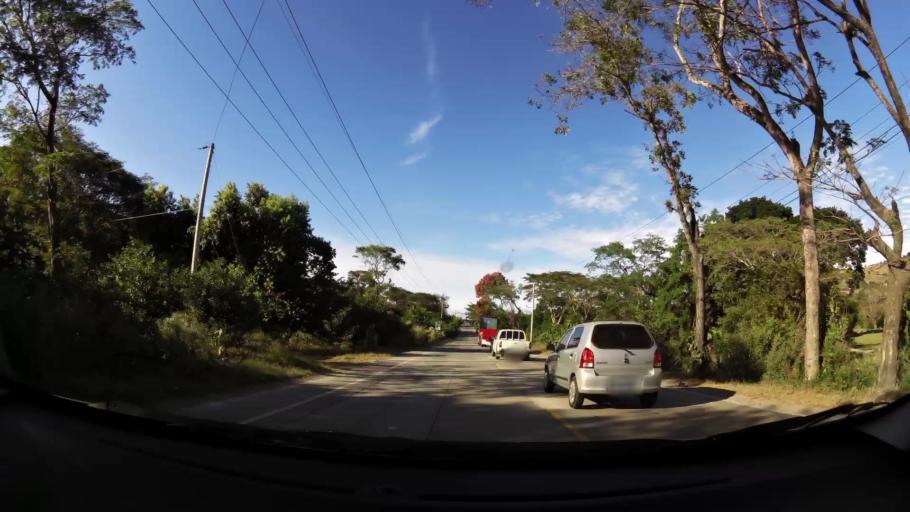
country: SV
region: Santa Ana
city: Metapan
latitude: 14.2840
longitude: -89.4617
